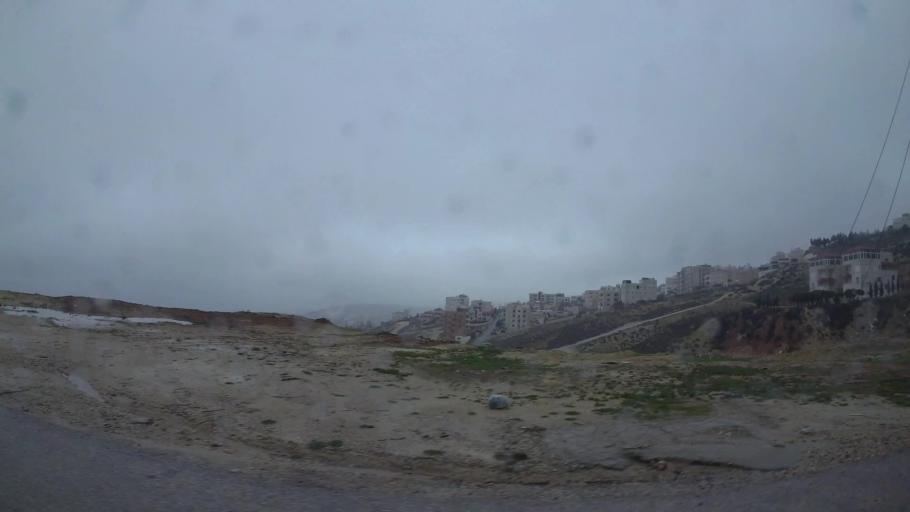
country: JO
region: Amman
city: Al Jubayhah
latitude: 32.0364
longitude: 35.8540
